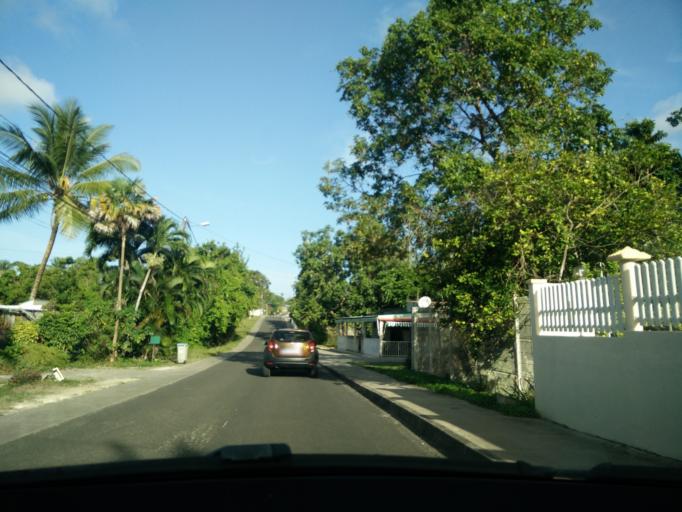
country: GP
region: Guadeloupe
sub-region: Guadeloupe
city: Sainte-Anne
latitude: 16.2787
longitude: -61.4068
